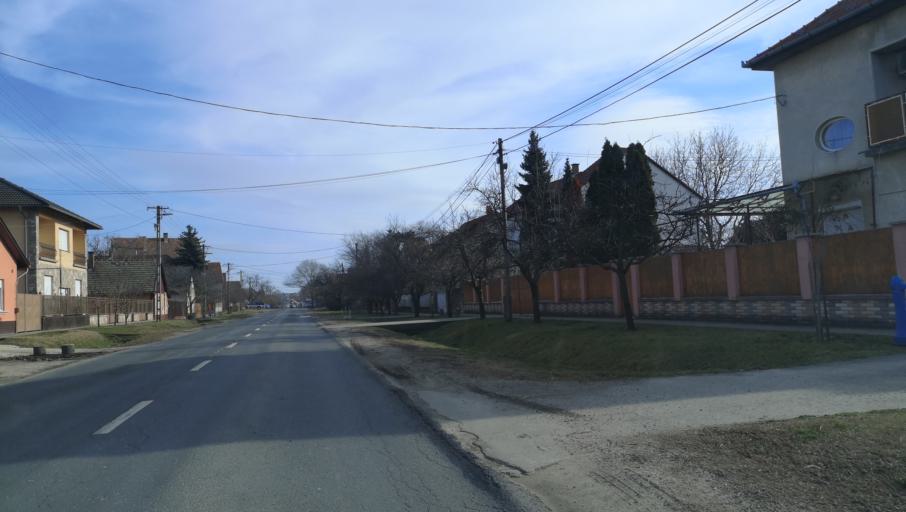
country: HU
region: Pest
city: Monor
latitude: 47.3583
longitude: 19.4388
